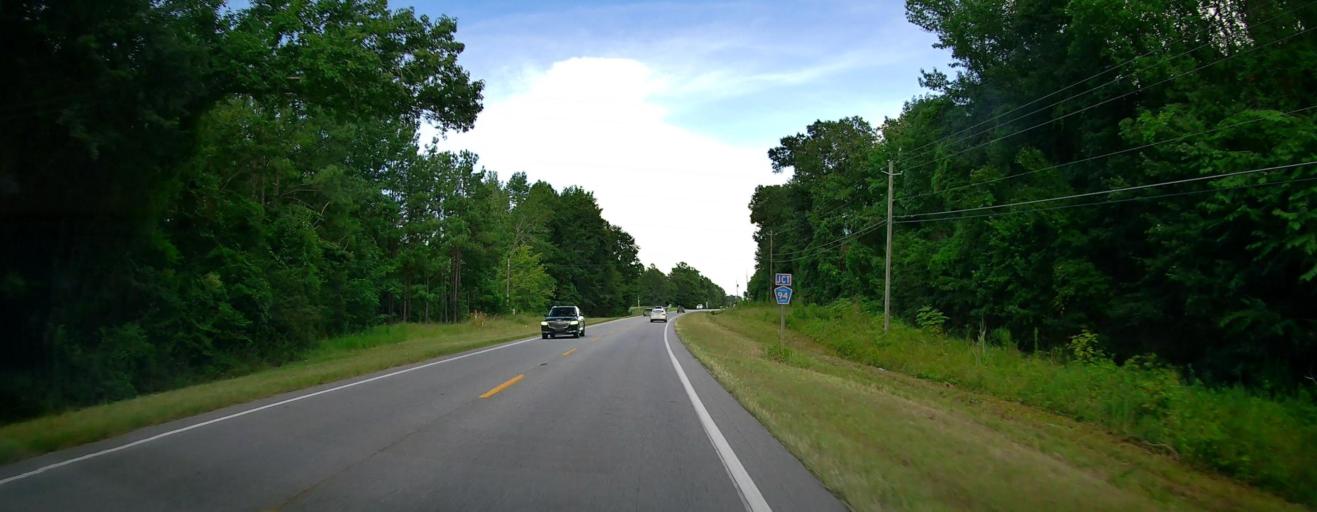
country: US
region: Alabama
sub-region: Russell County
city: Ladonia
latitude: 32.4616
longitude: -85.1705
